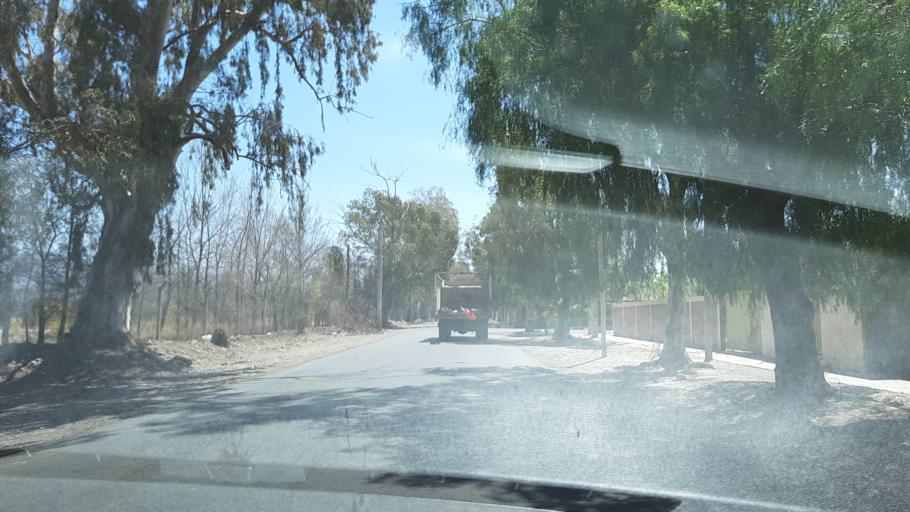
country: AR
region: San Juan
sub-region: Departamento de Zonda
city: Zonda
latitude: -31.5387
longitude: -68.7525
